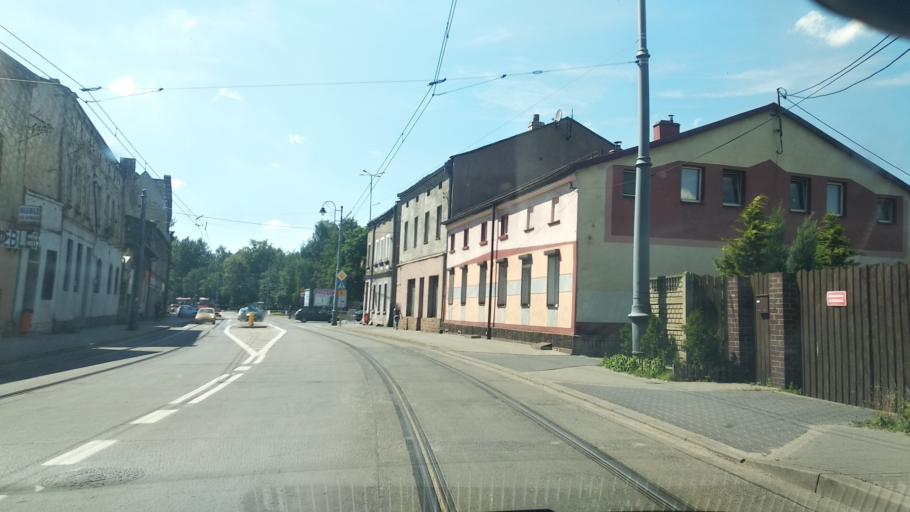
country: PL
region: Silesian Voivodeship
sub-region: Sosnowiec
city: Sosnowiec
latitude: 50.2682
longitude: 19.0823
